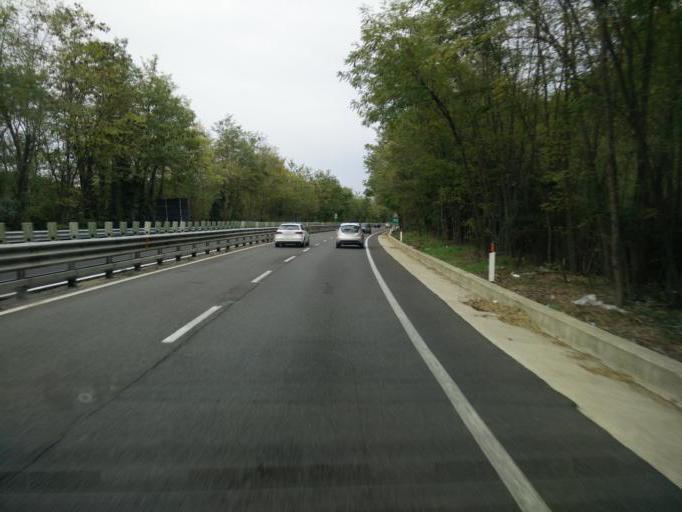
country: IT
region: Tuscany
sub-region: Province of Florence
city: Barberino Val d'Elsa
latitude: 43.5105
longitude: 11.1909
